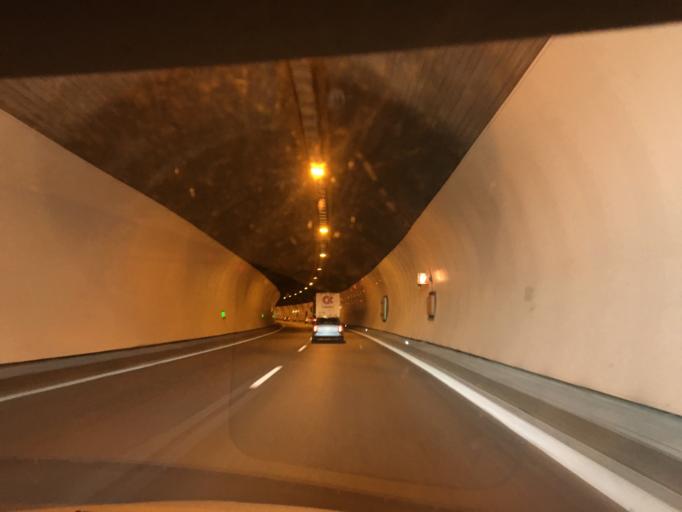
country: DE
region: Baden-Wuerttemberg
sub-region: Tuebingen Region
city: Ulm
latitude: 48.4156
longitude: 9.9715
